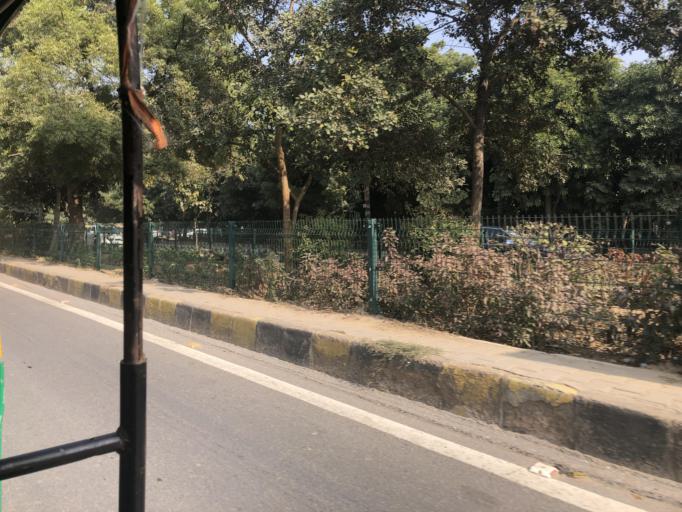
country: IN
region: Haryana
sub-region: Gurgaon
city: Gurgaon
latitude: 28.4315
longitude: 77.0912
